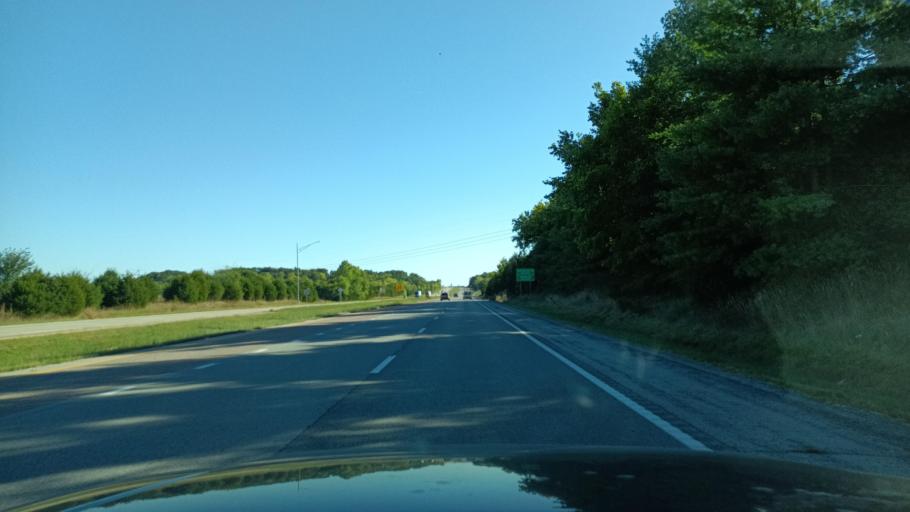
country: US
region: Missouri
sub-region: Boone County
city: Columbia
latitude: 39.0593
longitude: -92.3307
